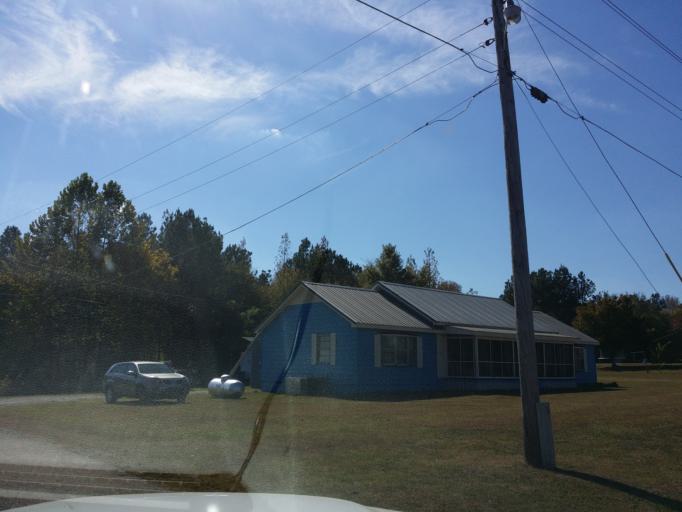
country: US
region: Mississippi
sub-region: Alcorn County
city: Corinth
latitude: 34.9819
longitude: -88.5282
